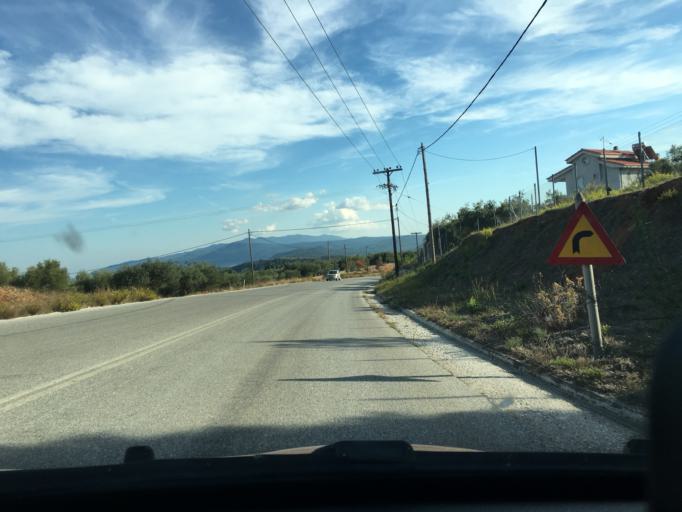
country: GR
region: Central Macedonia
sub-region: Nomos Chalkidikis
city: Agios Nikolaos
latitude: 40.2655
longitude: 23.6972
